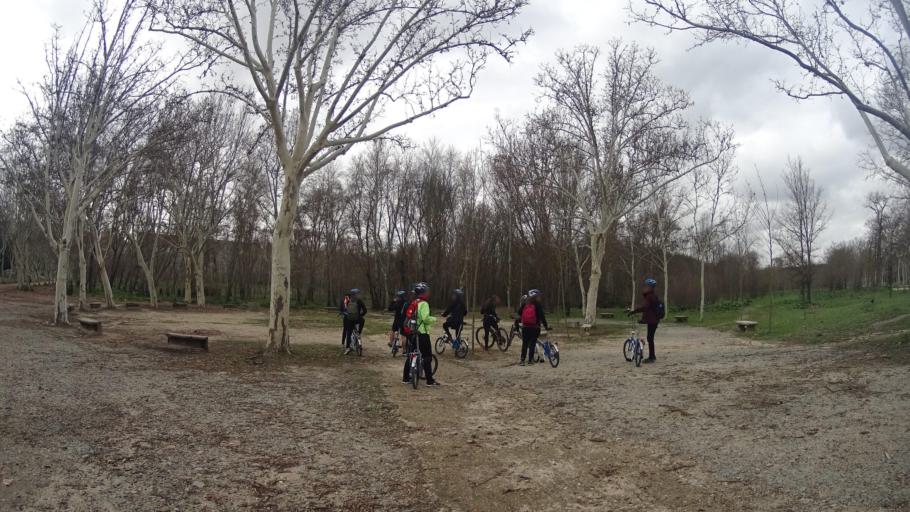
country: ES
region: Madrid
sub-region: Provincia de Madrid
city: Moncloa-Aravaca
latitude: 40.4189
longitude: -3.7383
